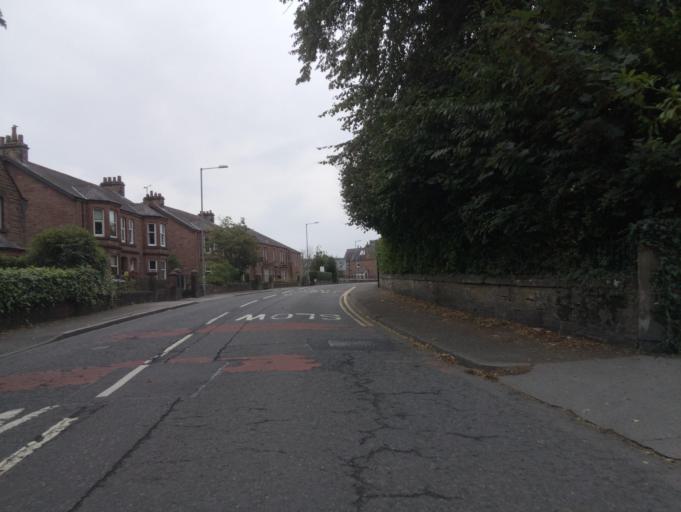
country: GB
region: Scotland
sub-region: Dumfries and Galloway
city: Dumfries
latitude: 55.0743
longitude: -3.5990
